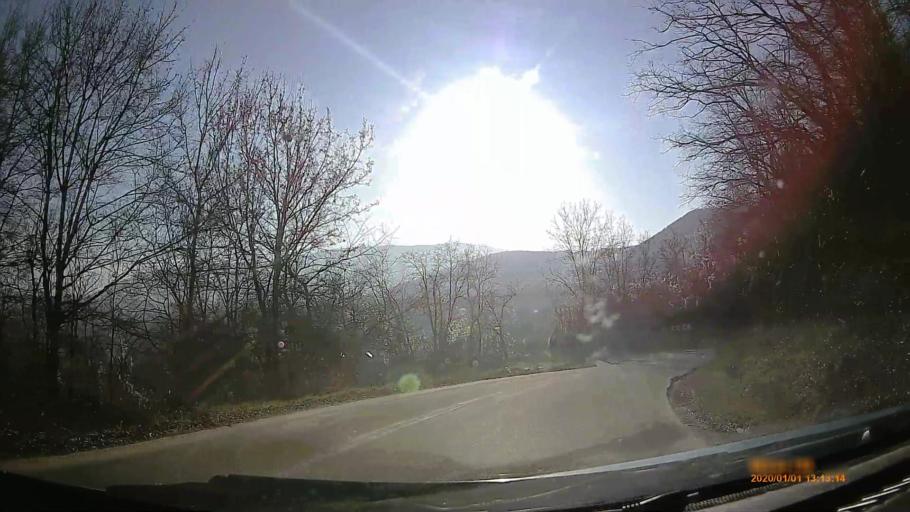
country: HU
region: Heves
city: Parad
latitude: 47.9274
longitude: 20.0225
